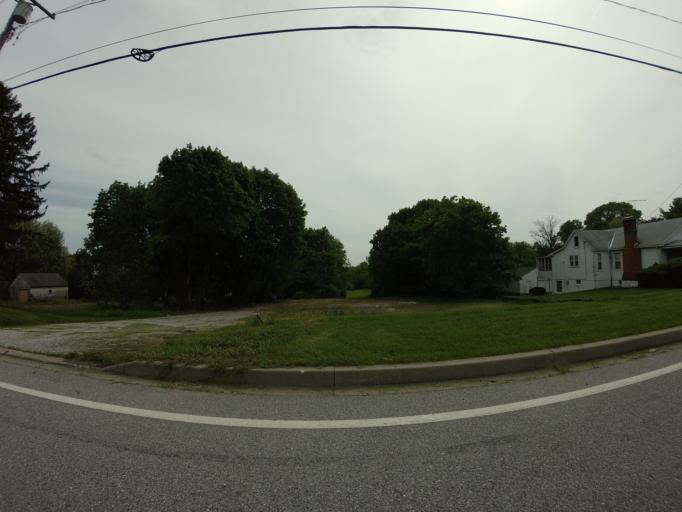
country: US
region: Maryland
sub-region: Baltimore County
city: Reisterstown
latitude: 39.4723
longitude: -76.8347
